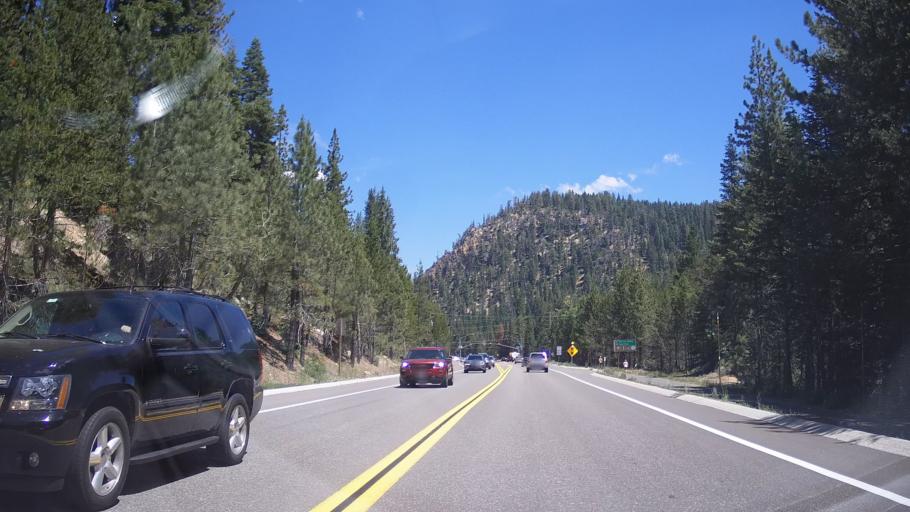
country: US
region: California
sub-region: Placer County
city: Sunnyside-Tahoe City
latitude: 39.2021
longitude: -120.2008
